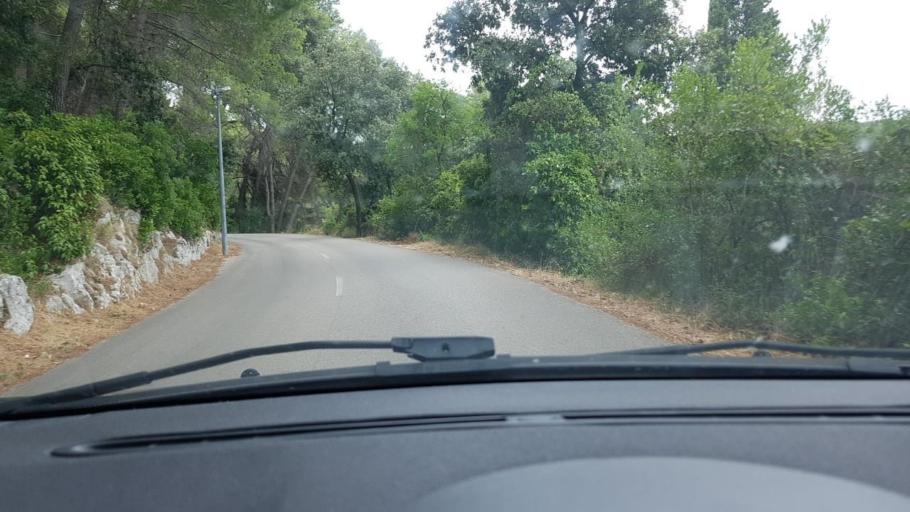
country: HR
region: Dubrovacko-Neretvanska
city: Korcula
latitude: 42.9606
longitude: 17.1275
